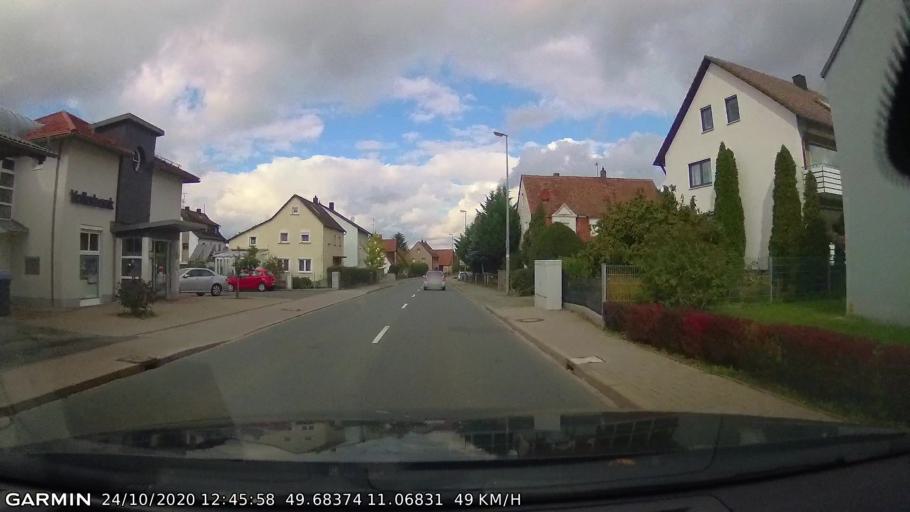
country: DE
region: Bavaria
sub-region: Upper Franconia
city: Poxdorf
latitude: 49.6838
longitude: 11.0683
